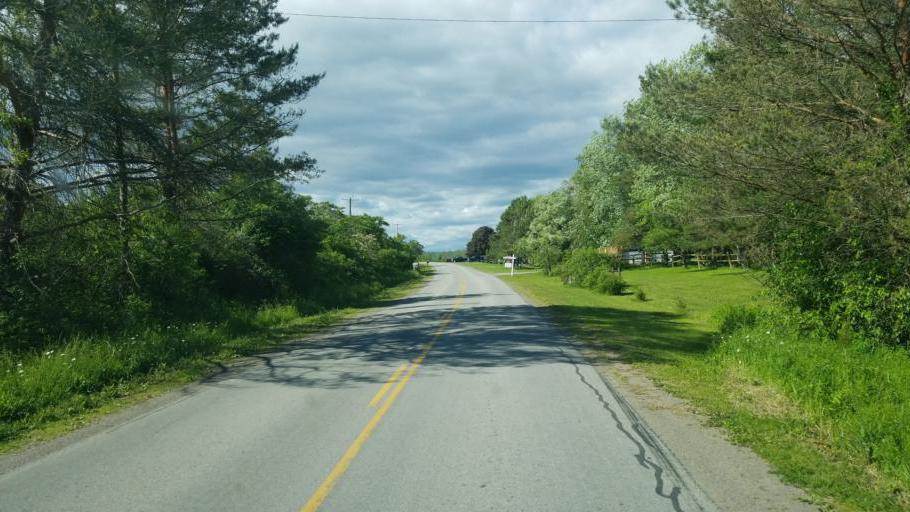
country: US
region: New York
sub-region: Montgomery County
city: Fort Plain
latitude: 42.9500
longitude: -74.6356
